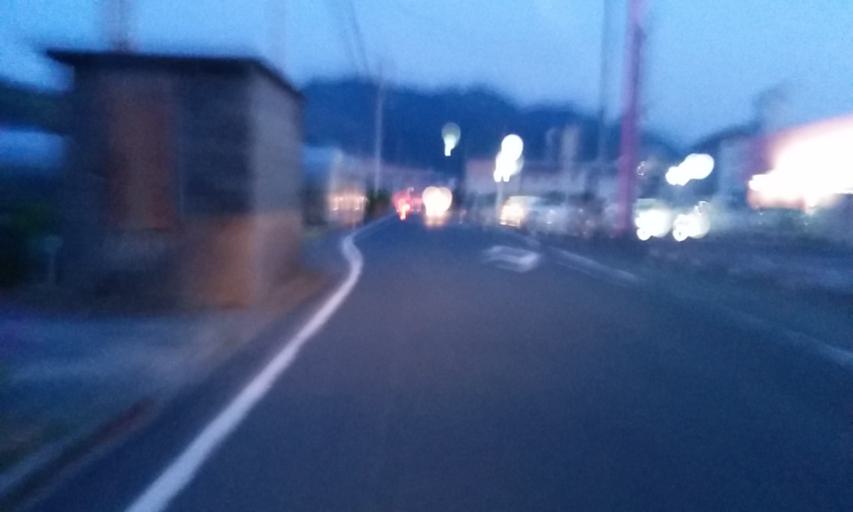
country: JP
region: Ehime
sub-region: Nishiuwa-gun
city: Ikata-cho
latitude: 33.4886
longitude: 132.3990
